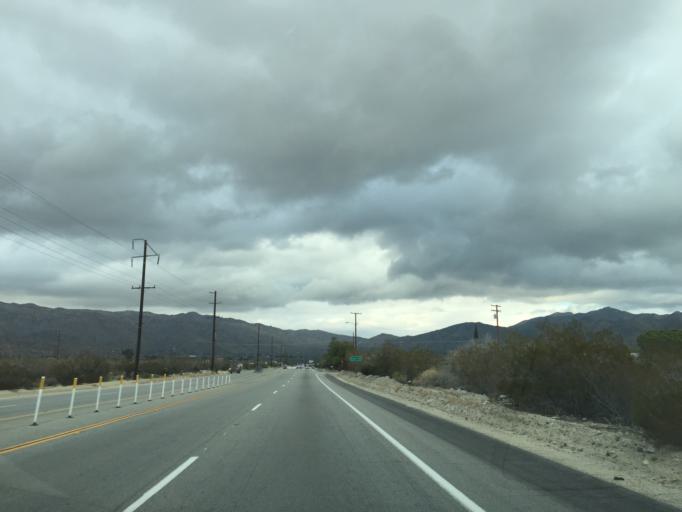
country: US
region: California
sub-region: San Bernardino County
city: Morongo Valley
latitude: 34.0722
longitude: -116.5473
